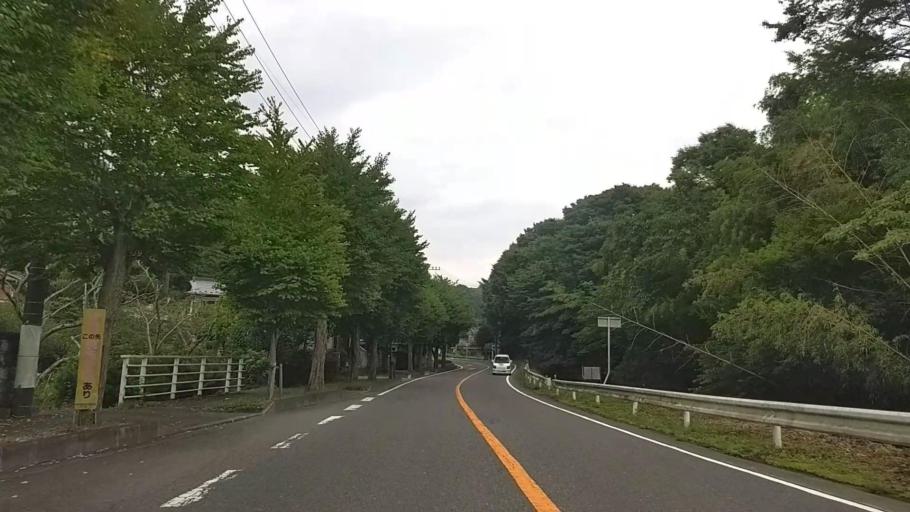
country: JP
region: Kanagawa
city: Hadano
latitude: 35.3360
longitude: 139.1983
